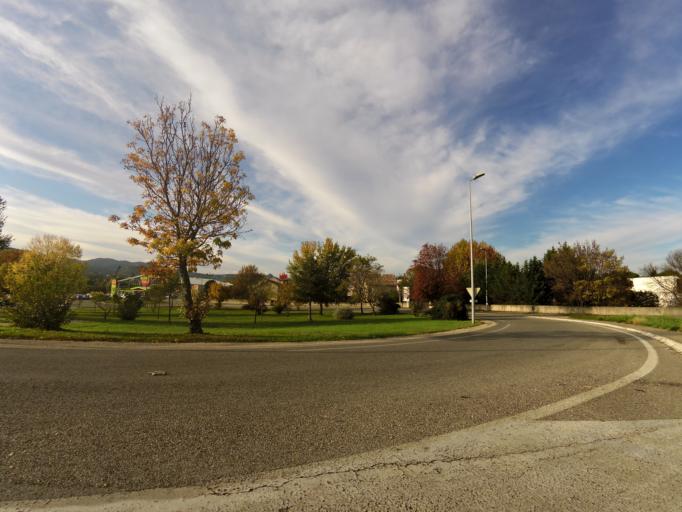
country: FR
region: Languedoc-Roussillon
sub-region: Departement du Gard
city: Ales
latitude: 44.1091
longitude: 4.1021
